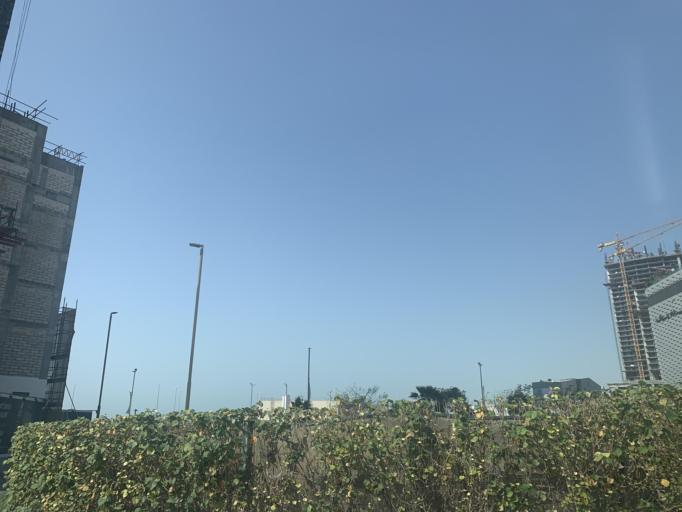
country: BH
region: Manama
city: Manama
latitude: 26.2454
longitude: 50.5763
